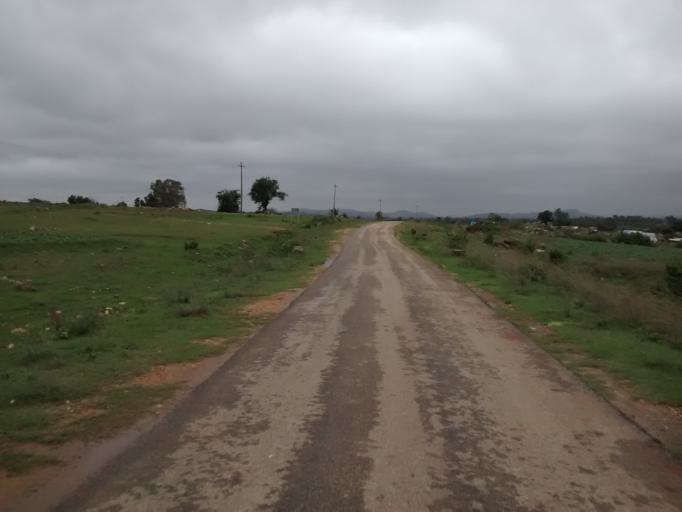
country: IN
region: Karnataka
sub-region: Hassan
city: Hassan
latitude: 12.9371
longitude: 76.1752
